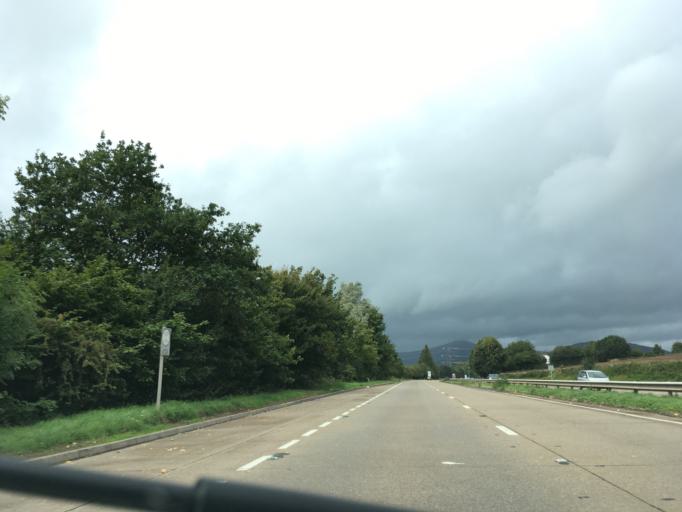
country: GB
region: Wales
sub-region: Monmouthshire
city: Abergavenny
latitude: 51.8015
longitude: -3.0024
